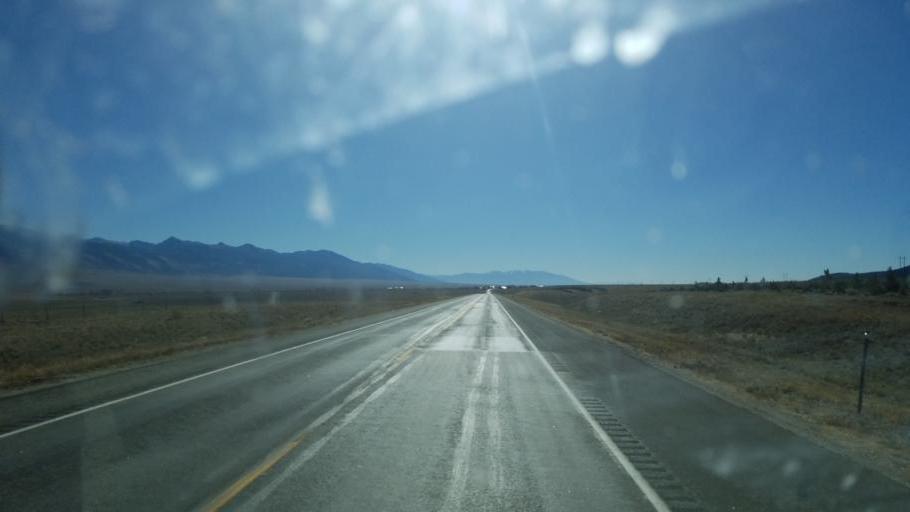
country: US
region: Colorado
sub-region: Saguache County
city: Saguache
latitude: 38.2756
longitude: -105.9700
